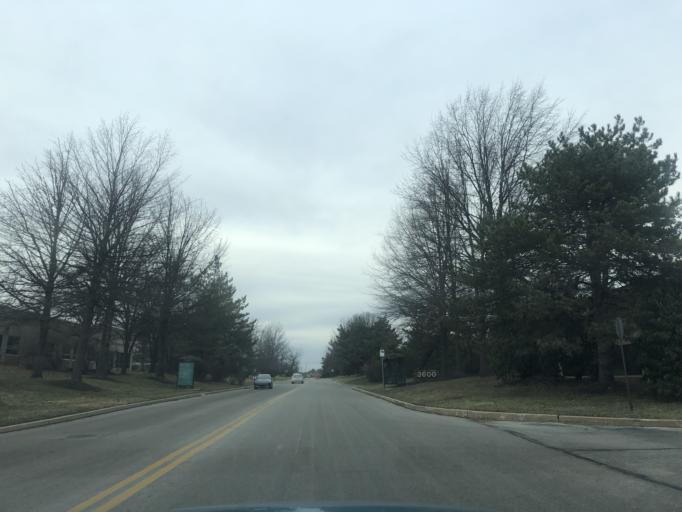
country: US
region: Pennsylvania
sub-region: Montgomery County
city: Bridgeport
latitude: 40.0884
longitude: -75.3407
